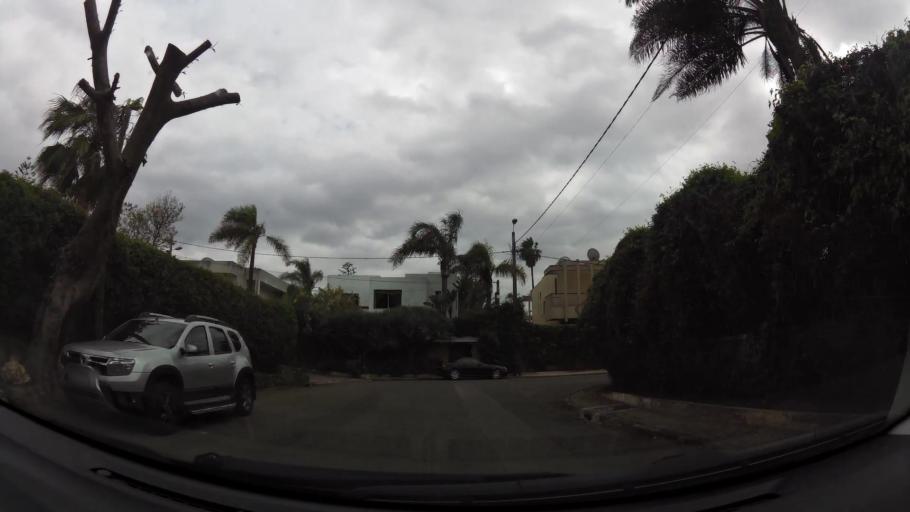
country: MA
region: Grand Casablanca
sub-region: Casablanca
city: Casablanca
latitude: 33.5731
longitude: -7.6592
